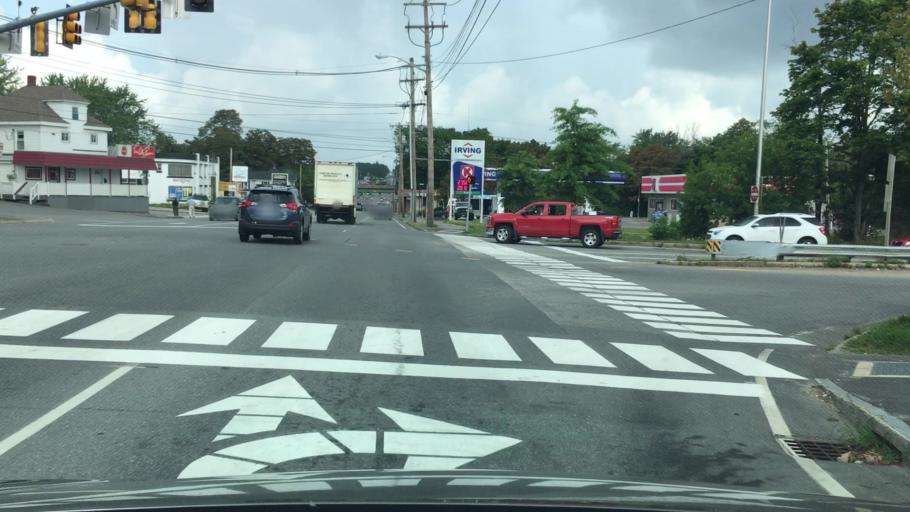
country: US
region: Maine
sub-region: Penobscot County
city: Bangor
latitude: 44.8176
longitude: -68.7737
